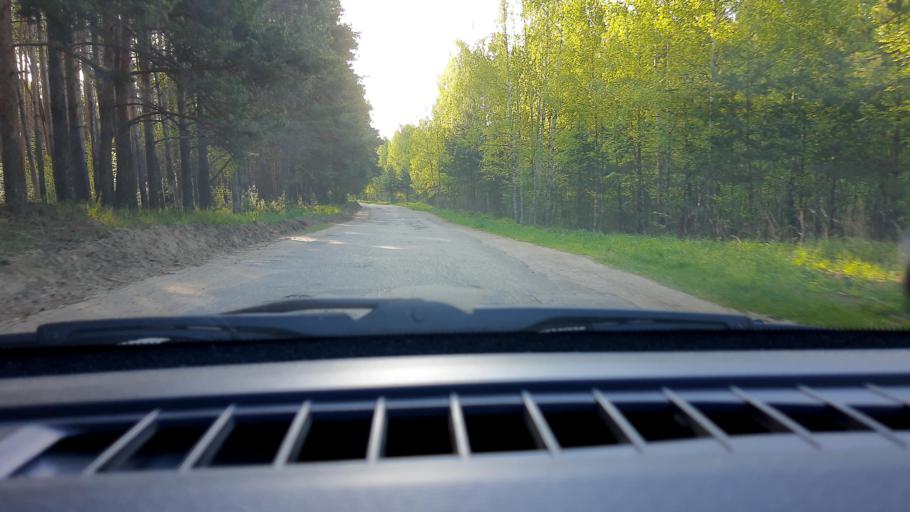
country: RU
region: Nizjnij Novgorod
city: Sitniki
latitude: 56.4151
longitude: 44.0508
